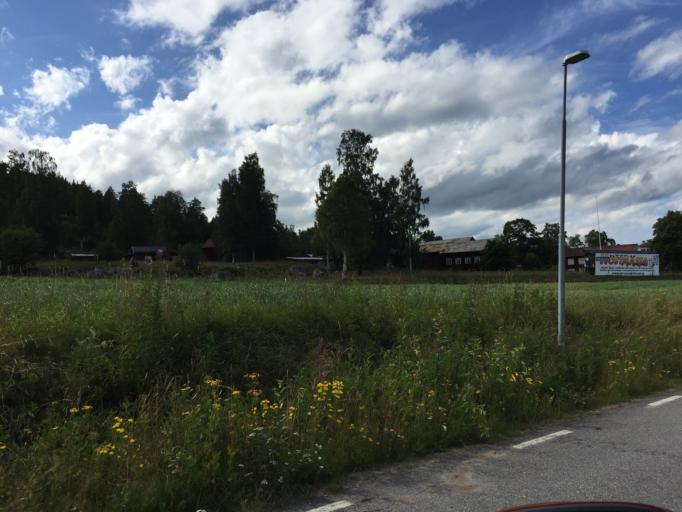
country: SE
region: Gaevleborg
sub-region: Ljusdals Kommun
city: Jaervsoe
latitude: 61.7456
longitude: 16.1604
